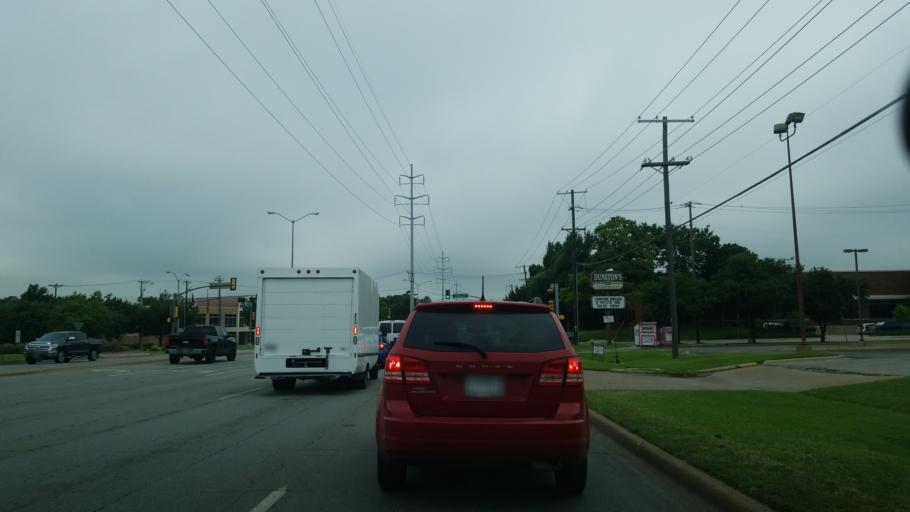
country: US
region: Texas
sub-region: Dallas County
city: University Park
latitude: 32.8368
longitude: -96.8648
